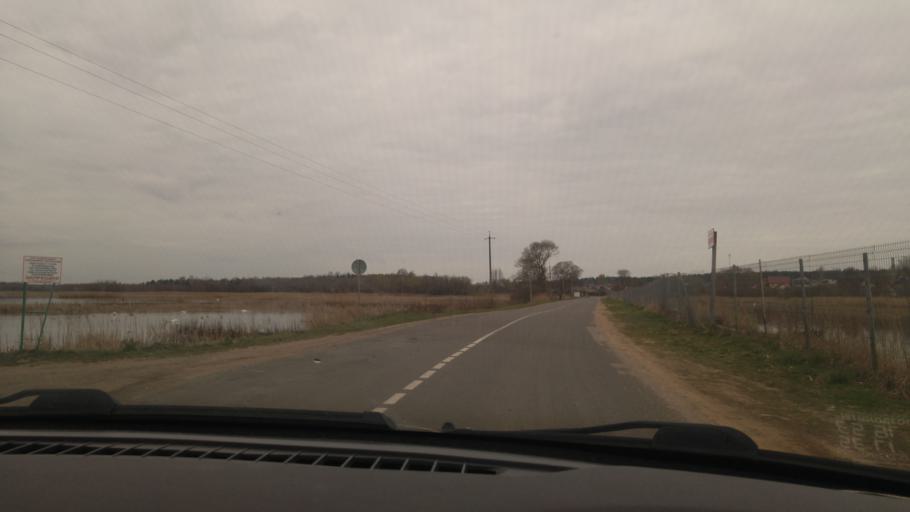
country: BY
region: Minsk
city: Smilavichy
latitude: 53.7176
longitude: 28.1427
